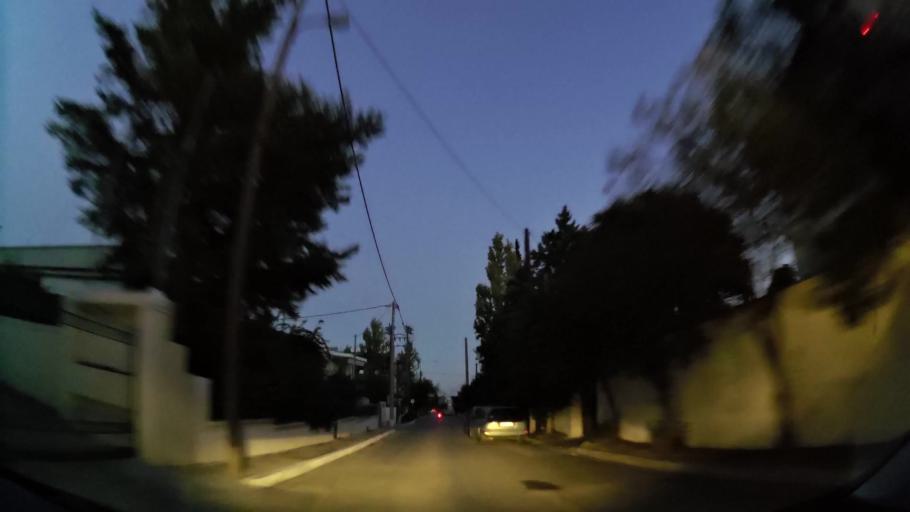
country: GR
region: Attica
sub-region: Nomarchia Anatolikis Attikis
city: Paiania
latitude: 37.9537
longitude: 23.8559
